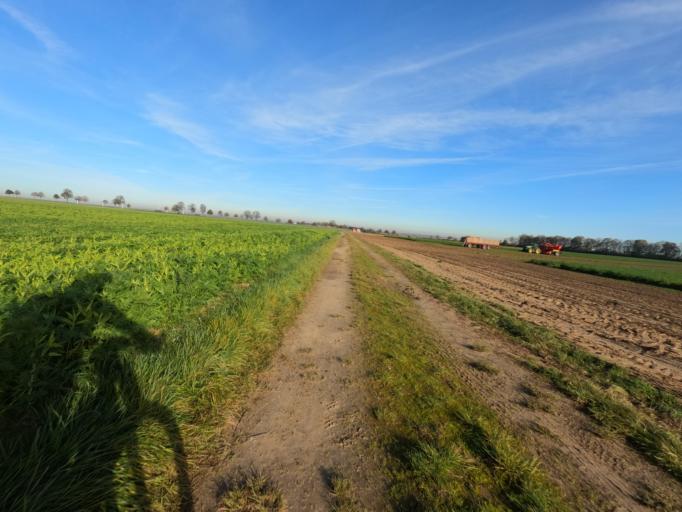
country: DE
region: North Rhine-Westphalia
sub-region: Regierungsbezirk Koln
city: Titz
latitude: 51.0427
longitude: 6.4252
